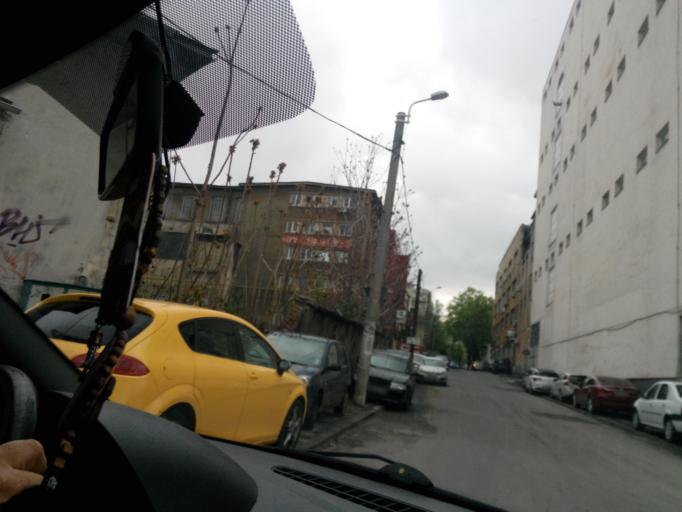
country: RO
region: Bucuresti
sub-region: Municipiul Bucuresti
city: Bucharest
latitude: 44.4177
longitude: 26.1163
